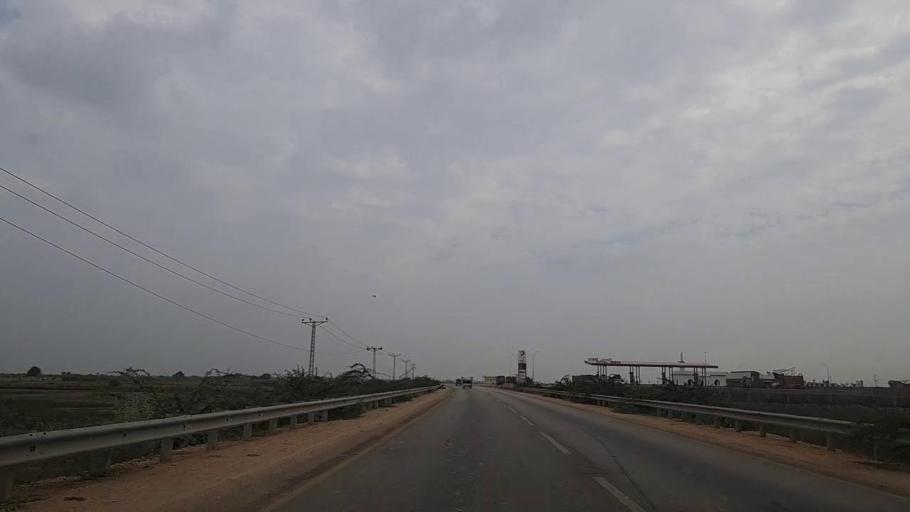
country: PK
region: Sindh
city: Thatta
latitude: 24.6155
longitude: 68.0589
